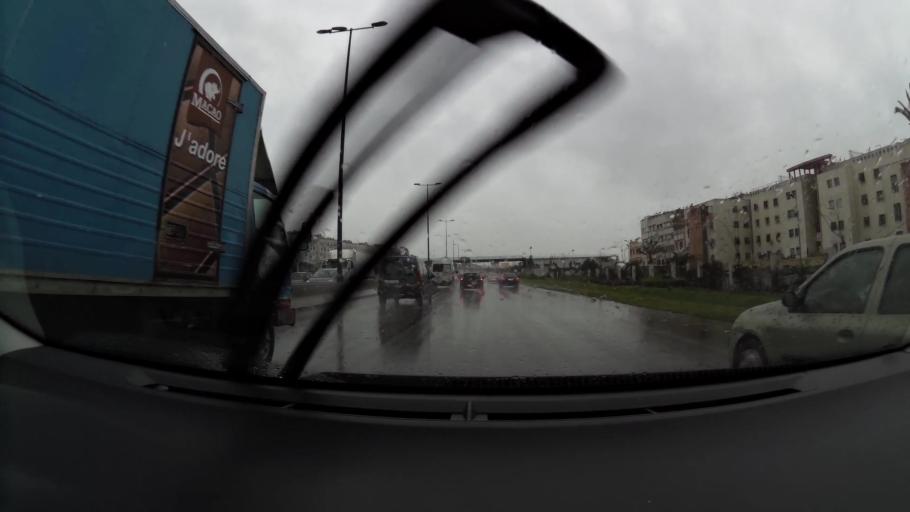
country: MA
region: Grand Casablanca
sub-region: Casablanca
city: Casablanca
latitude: 33.5628
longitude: -7.5838
